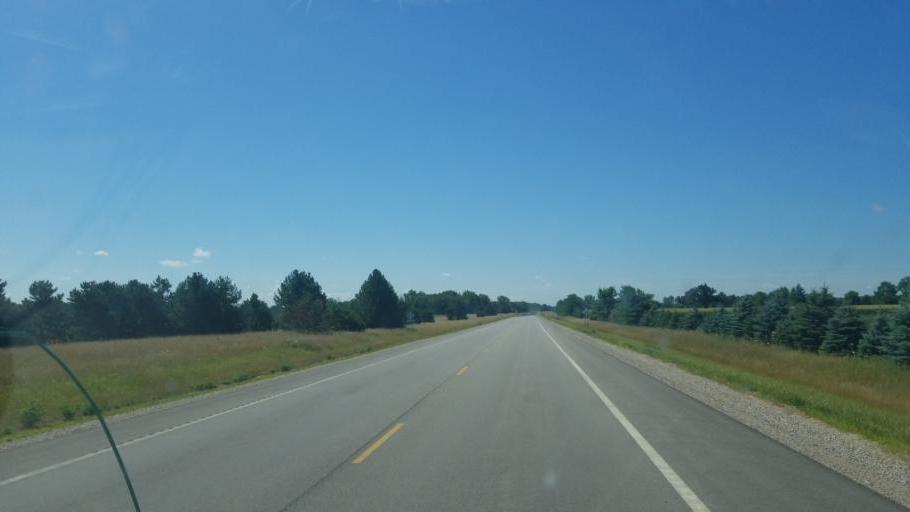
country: US
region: Ohio
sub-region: Van Wert County
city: Van Wert
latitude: 40.8754
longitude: -84.6251
